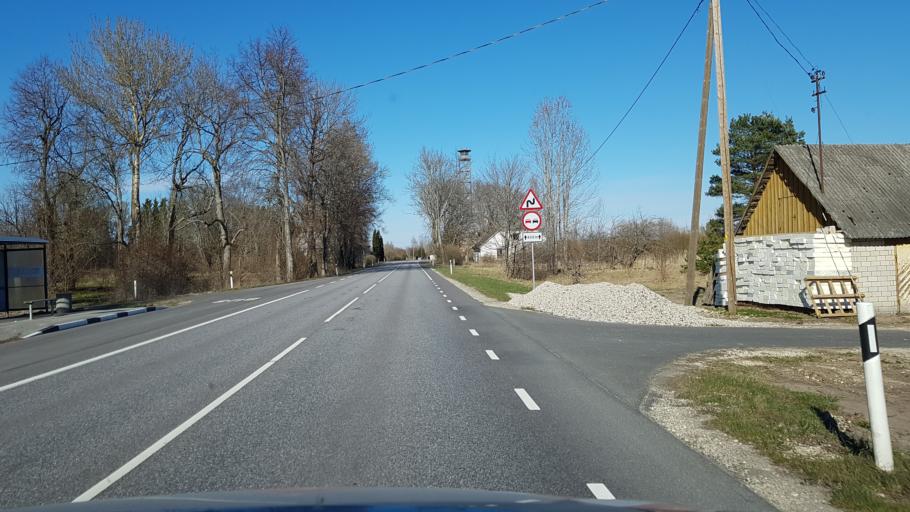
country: EE
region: Jogevamaa
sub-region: Mustvee linn
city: Mustvee
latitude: 58.9026
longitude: 26.9900
